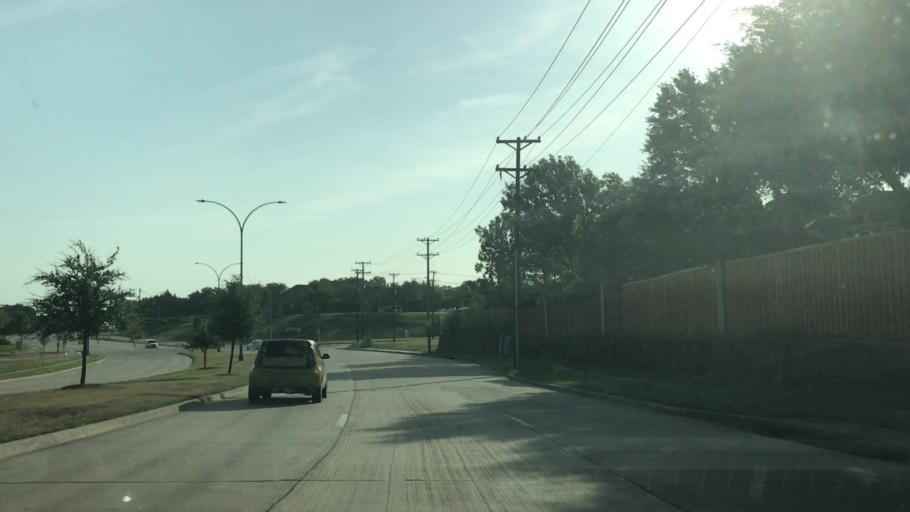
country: US
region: Texas
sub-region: Tarrant County
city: Arlington
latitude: 32.7764
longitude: -97.0762
